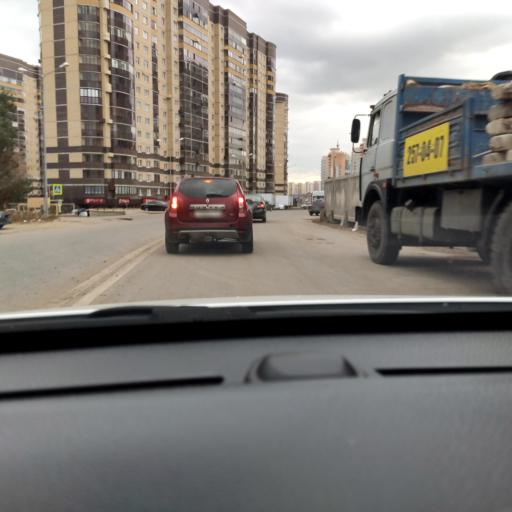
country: RU
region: Voronezj
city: Voronezh
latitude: 51.7167
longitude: 39.1917
